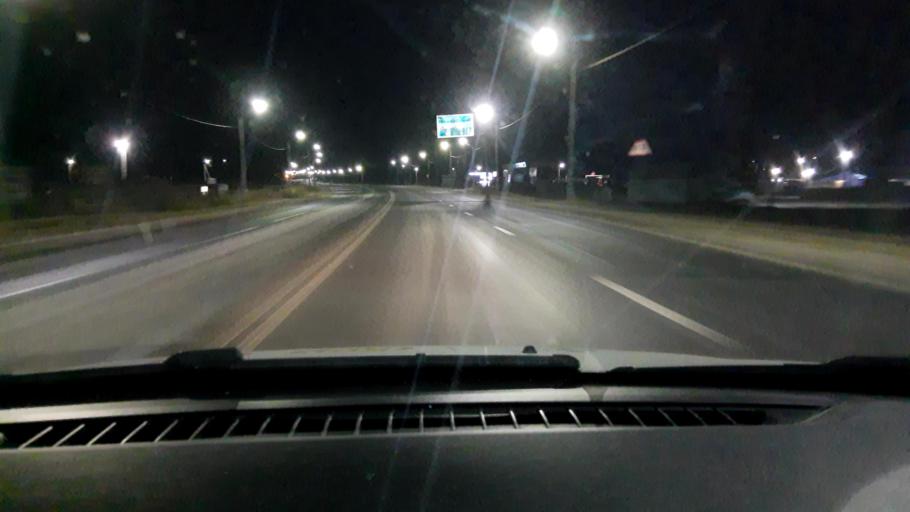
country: RU
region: Nizjnij Novgorod
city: Sitniki
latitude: 56.4994
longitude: 44.0254
